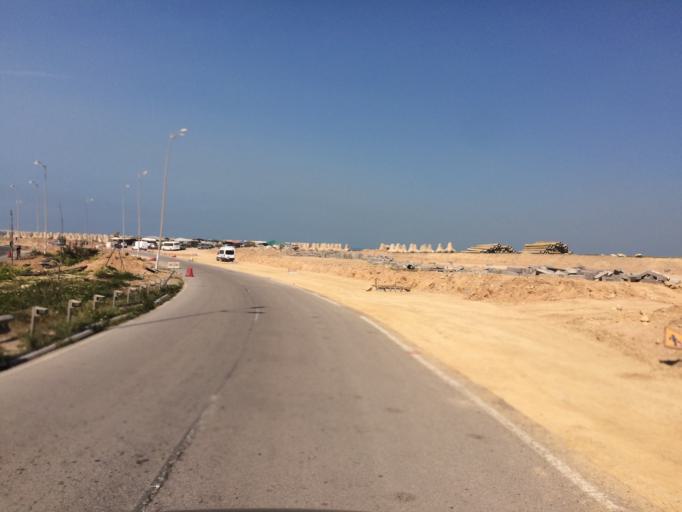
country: MA
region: Doukkala-Abda
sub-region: El-Jadida
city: Moulay Abdallah
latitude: 33.1381
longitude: -8.6123
